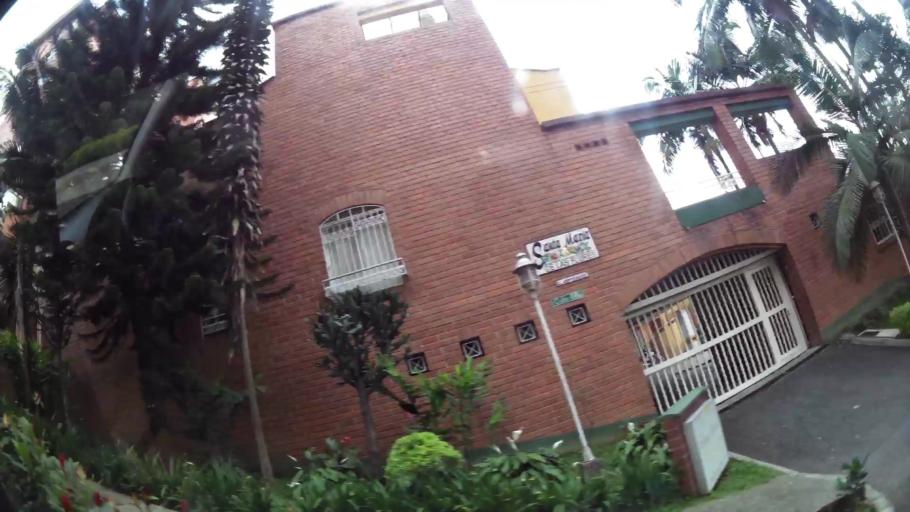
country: CO
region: Antioquia
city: Envigado
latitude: 6.1606
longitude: -75.6005
